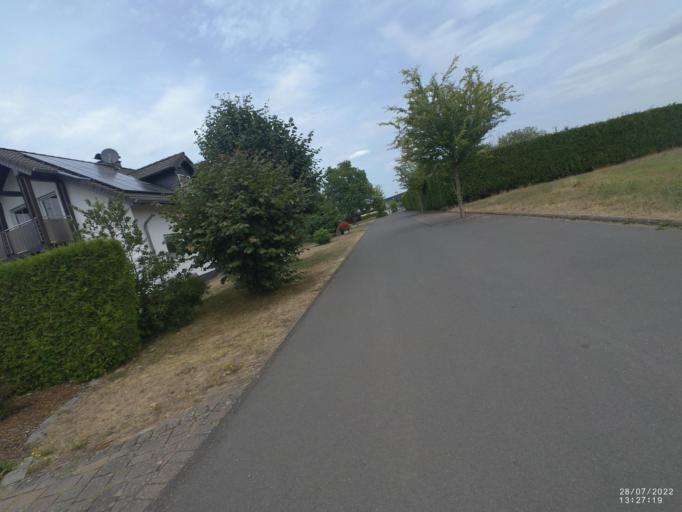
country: DE
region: Rheinland-Pfalz
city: Oberbettingen
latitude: 50.2833
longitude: 6.6314
